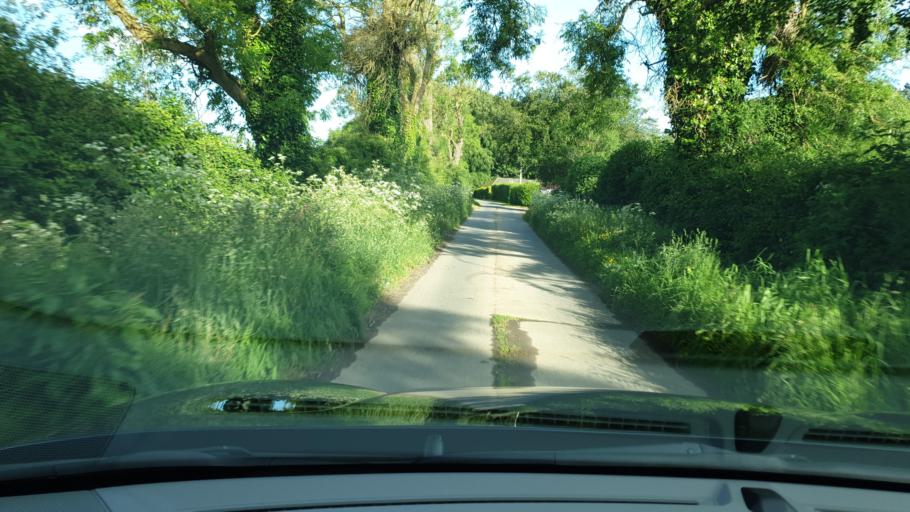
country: IE
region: Leinster
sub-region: An Mhi
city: Ashbourne
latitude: 53.5512
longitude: -6.4213
